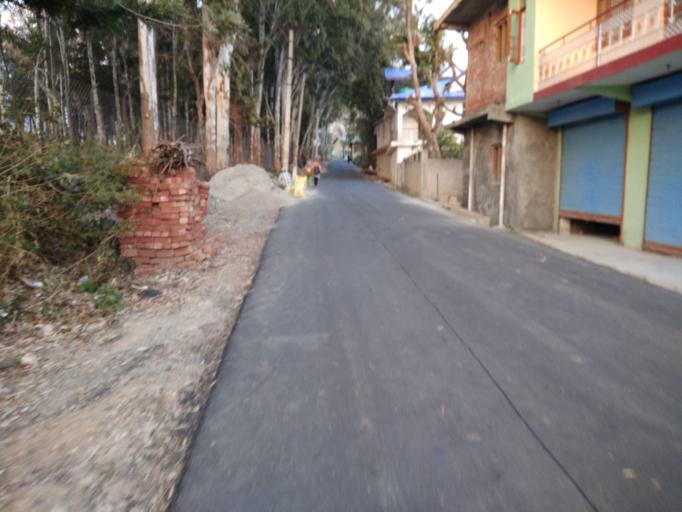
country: IN
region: Himachal Pradesh
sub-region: Kangra
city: Palampur
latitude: 32.1237
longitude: 76.5280
